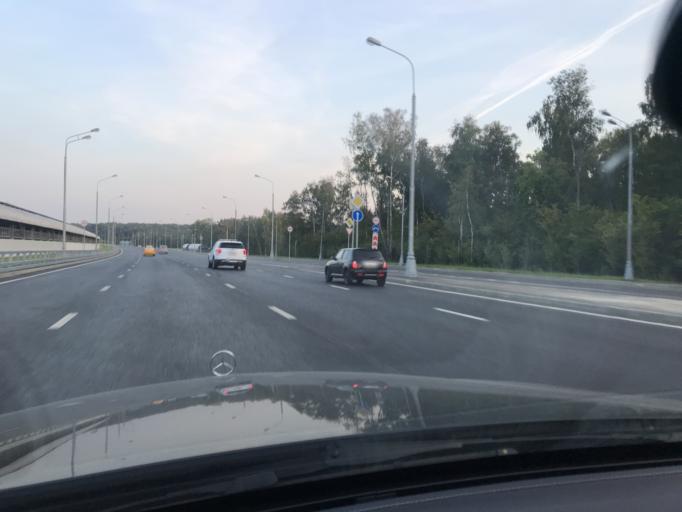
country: RU
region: Moskovskaya
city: Mosrentgen
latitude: 55.5930
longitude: 37.4199
